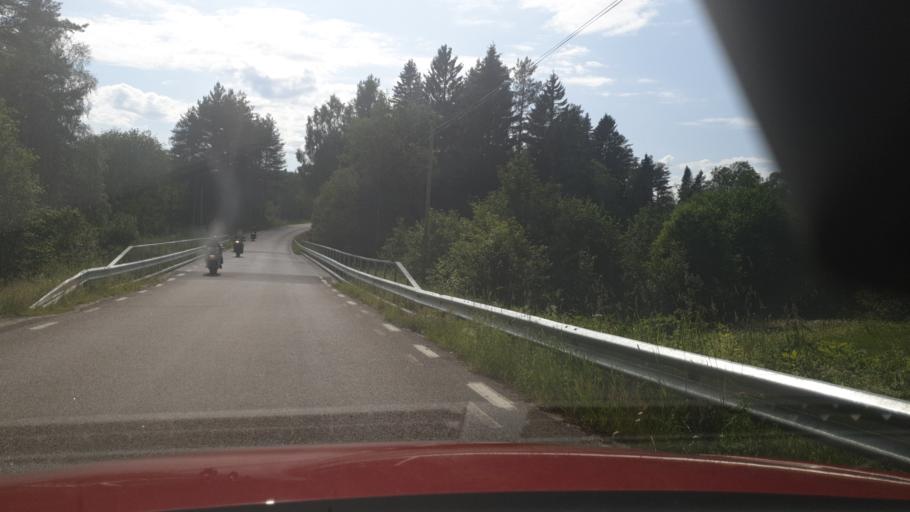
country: SE
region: Vaesternorrland
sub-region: Sundsvalls Kommun
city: Njurundabommen
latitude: 62.0366
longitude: 17.3425
